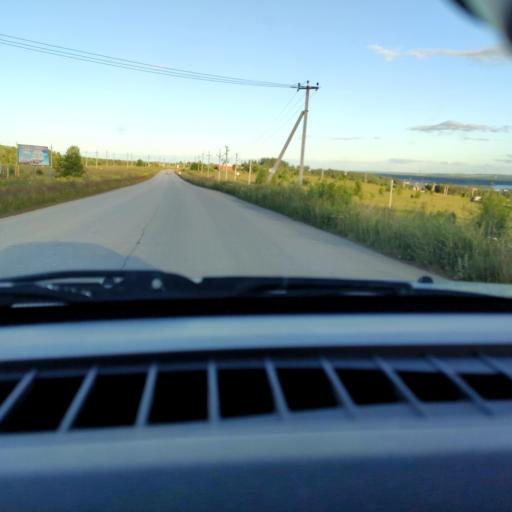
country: RU
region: Perm
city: Novyye Lyady
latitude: 58.1820
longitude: 56.5510
